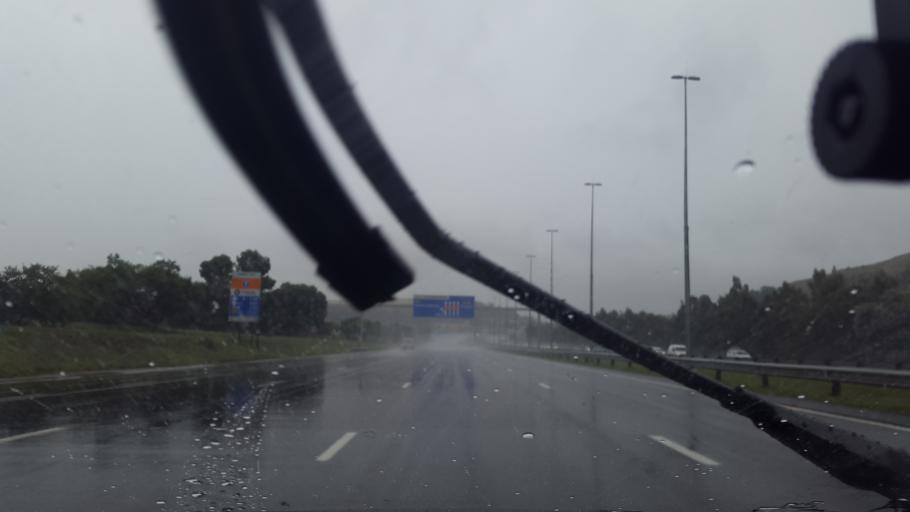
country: ZA
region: Gauteng
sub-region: City of Johannesburg Metropolitan Municipality
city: Johannesburg
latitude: -26.2432
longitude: 27.9625
